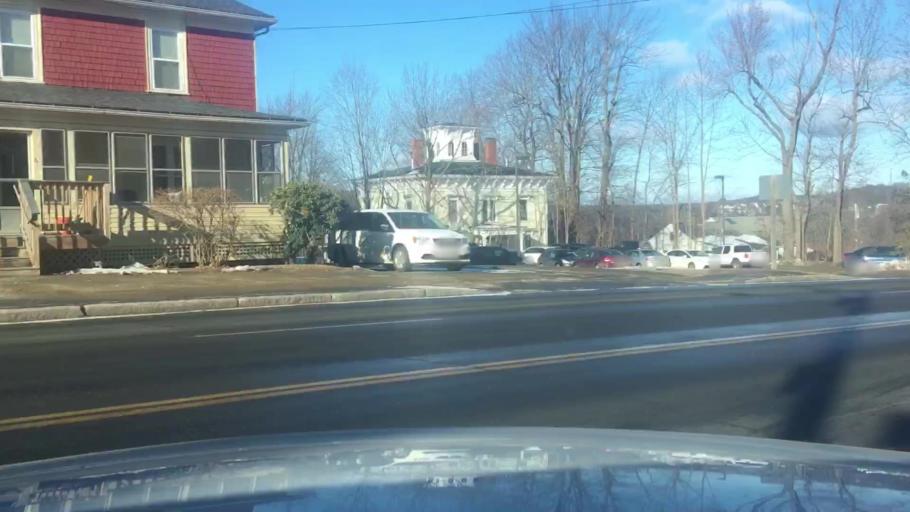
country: US
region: Maine
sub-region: Kennebec County
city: Augusta
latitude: 44.3111
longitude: -69.7645
